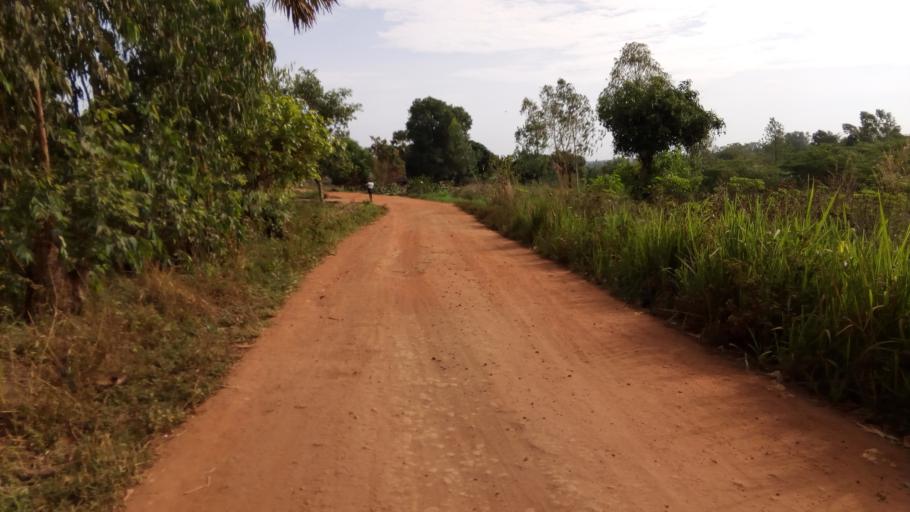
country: UG
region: Northern Region
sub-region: Gulu District
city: Gulu
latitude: 2.7955
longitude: 32.3237
